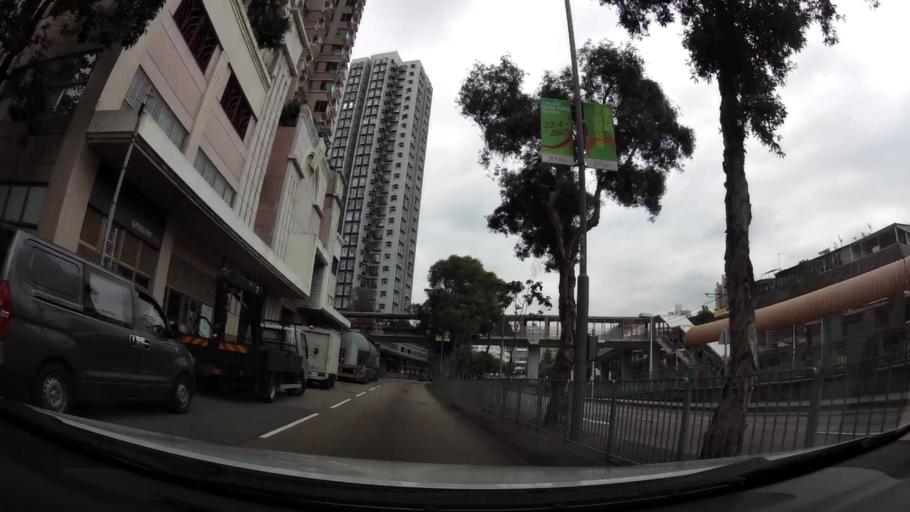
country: HK
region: Tuen Mun
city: Tuen Mun
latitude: 22.3975
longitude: 113.9772
